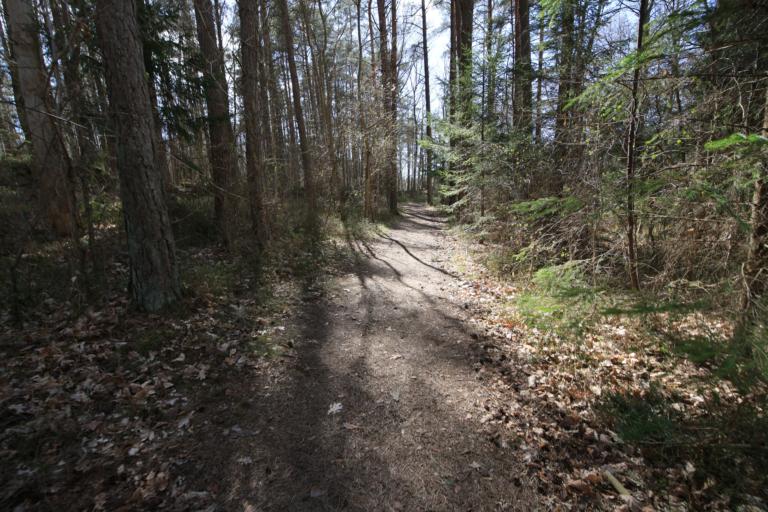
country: SE
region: Halland
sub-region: Varbergs Kommun
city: Varberg
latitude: 57.1800
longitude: 12.2393
